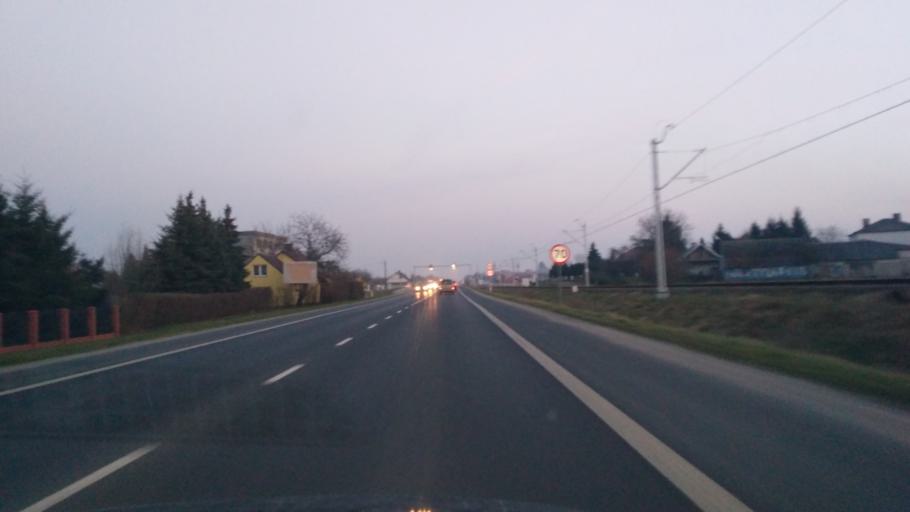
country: PL
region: Subcarpathian Voivodeship
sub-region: Powiat rzeszowski
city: Rudna Mala
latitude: 50.0899
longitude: 21.9822
